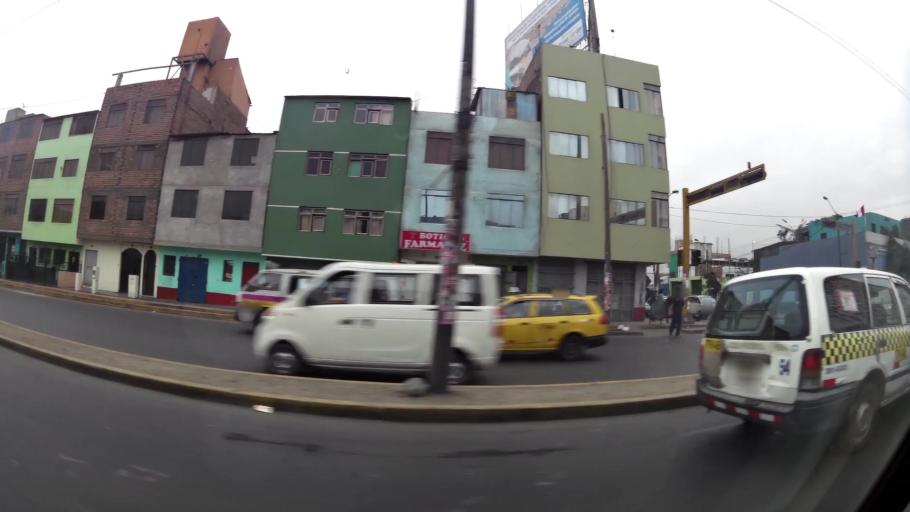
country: PE
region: Lima
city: Lima
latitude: -12.0471
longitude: -77.0507
